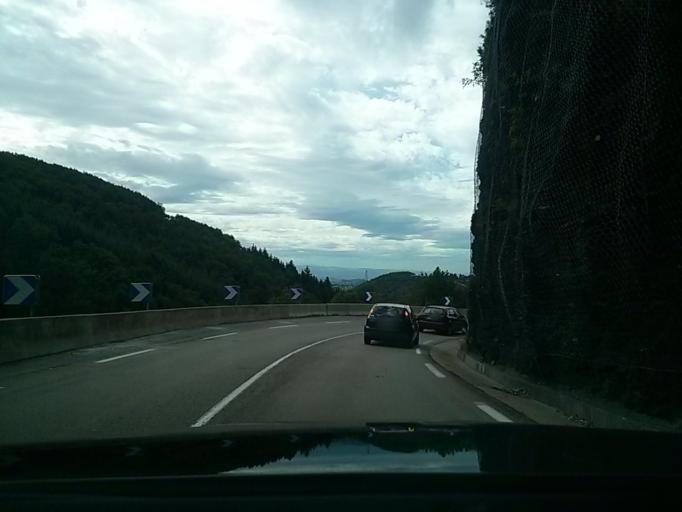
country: FR
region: Rhone-Alpes
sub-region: Departement de la Loire
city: Saint-Etienne
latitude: 45.3954
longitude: 4.4209
